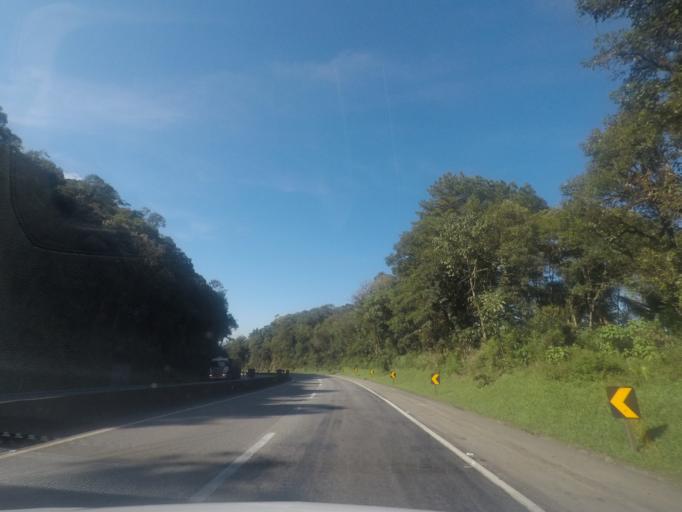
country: BR
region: Parana
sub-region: Piraquara
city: Piraquara
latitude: -25.5841
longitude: -48.9585
